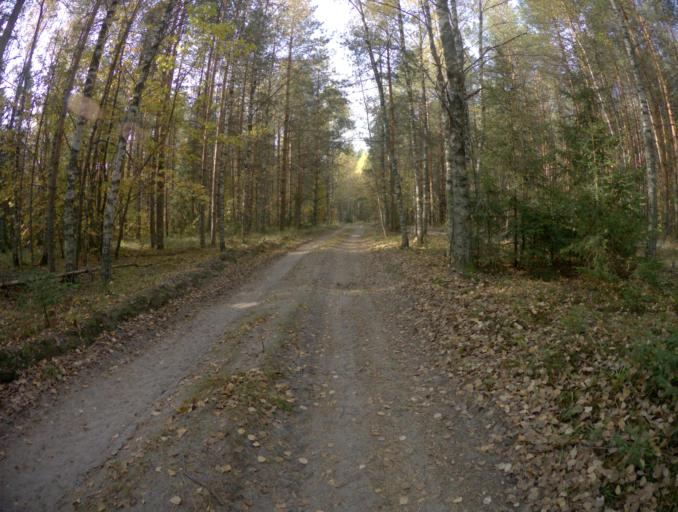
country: RU
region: Vladimir
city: Vorsha
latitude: 55.9549
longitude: 40.1433
